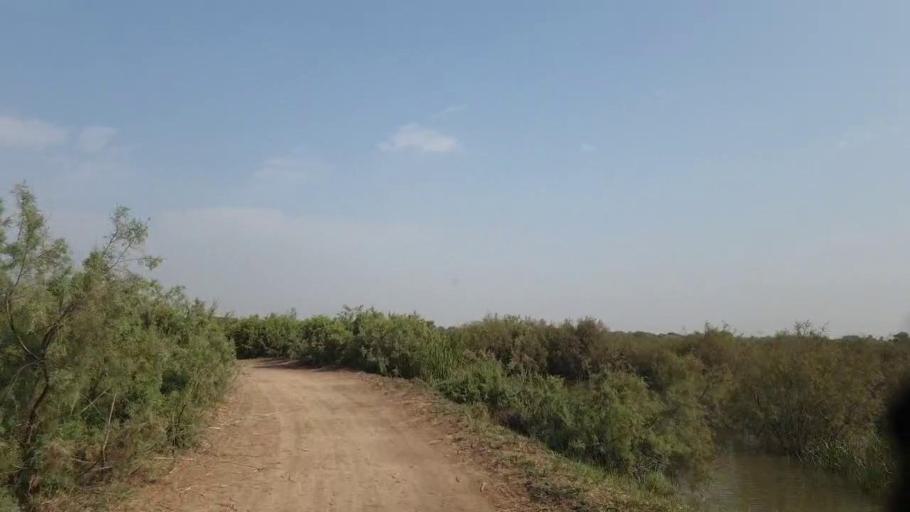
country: PK
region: Sindh
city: Tando Muhammad Khan
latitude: 25.0633
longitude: 68.4316
